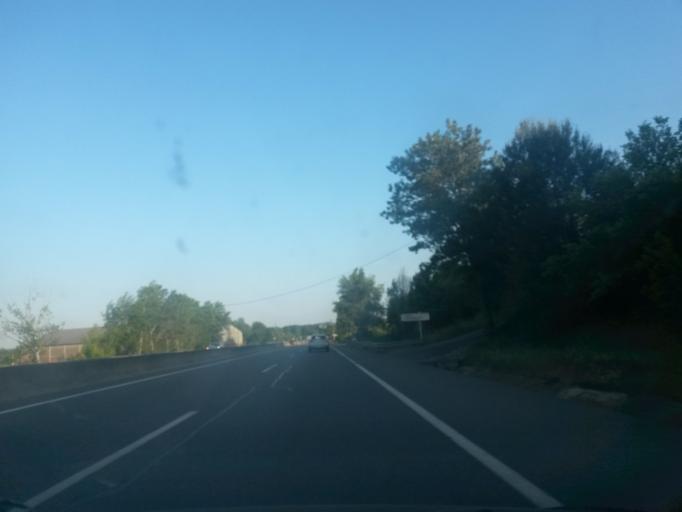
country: ES
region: Catalonia
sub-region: Provincia de Girona
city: Cornella del Terri
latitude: 42.0875
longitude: 2.8118
